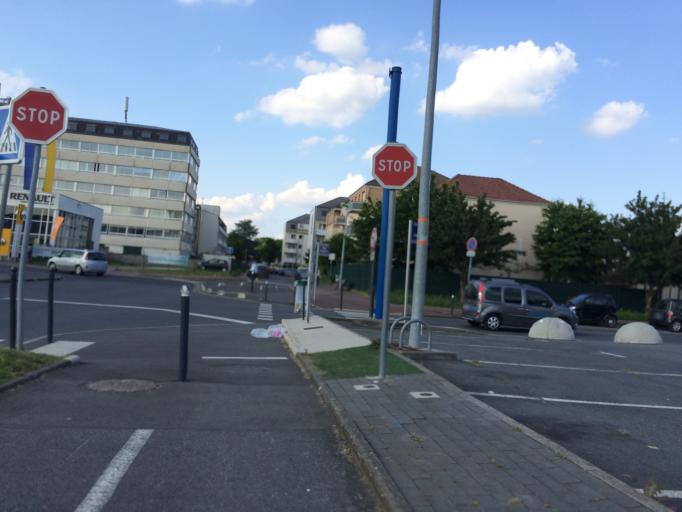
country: FR
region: Ile-de-France
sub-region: Departement de l'Essonne
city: Grigny
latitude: 48.6503
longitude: 2.3990
